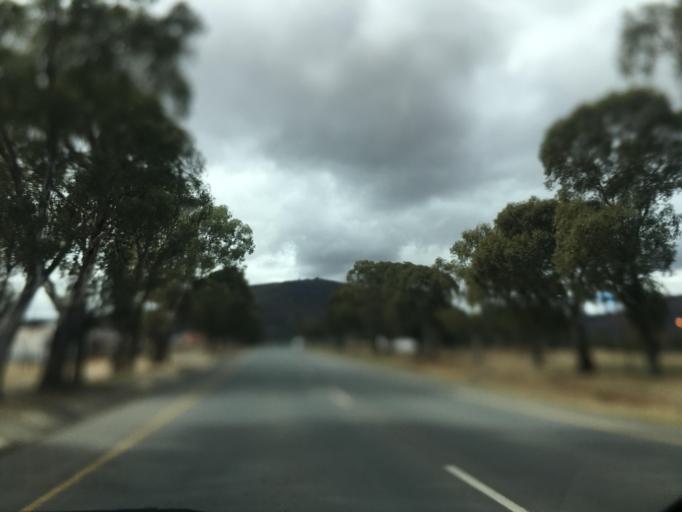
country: ZA
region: Eastern Cape
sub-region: Chris Hani District Municipality
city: Cala
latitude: -31.5284
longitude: 27.6851
